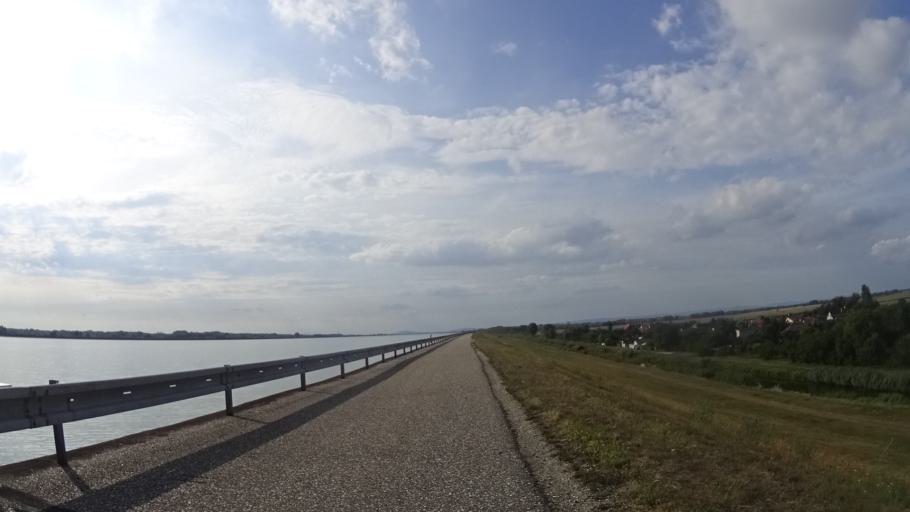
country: HU
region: Gyor-Moson-Sopron
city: Halaszi
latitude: 47.9495
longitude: 17.4401
